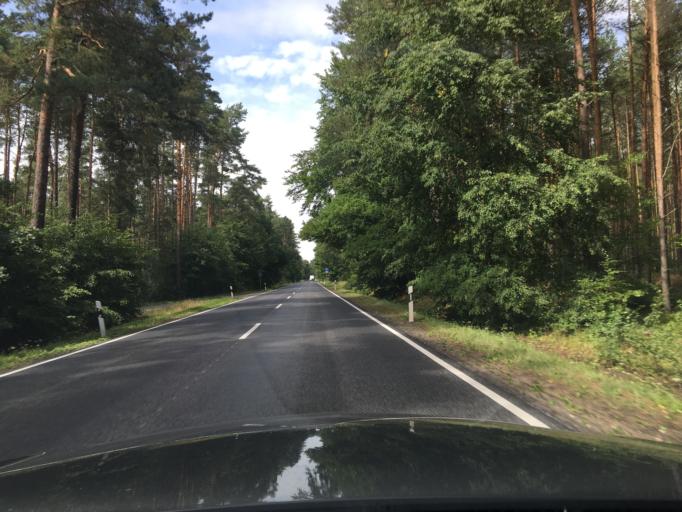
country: DE
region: Brandenburg
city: Furstenberg
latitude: 53.2128
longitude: 13.1282
